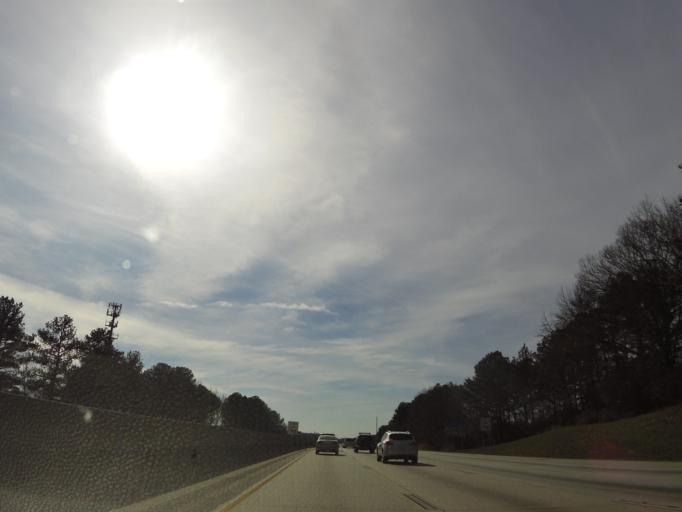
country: US
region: Georgia
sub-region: Fulton County
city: Union City
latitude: 33.5958
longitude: -84.4960
